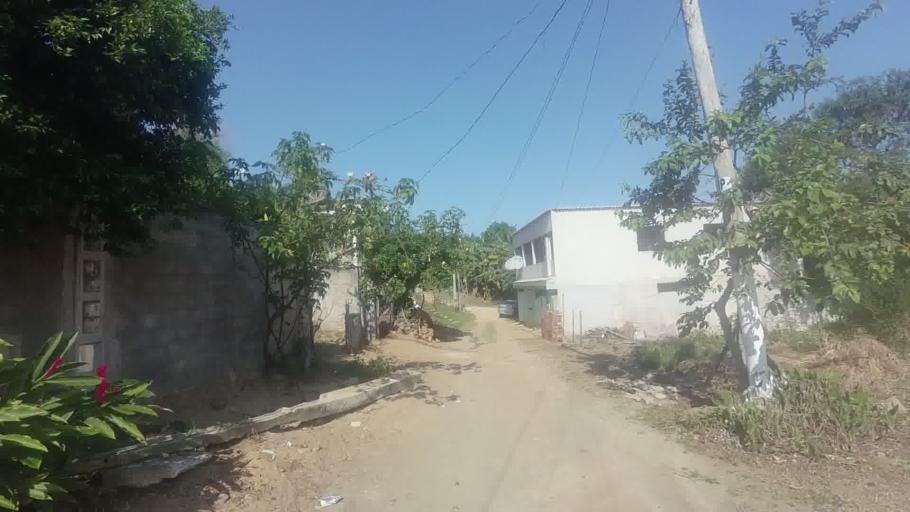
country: BR
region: Espirito Santo
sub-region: Piuma
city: Piuma
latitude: -20.8866
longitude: -40.7703
